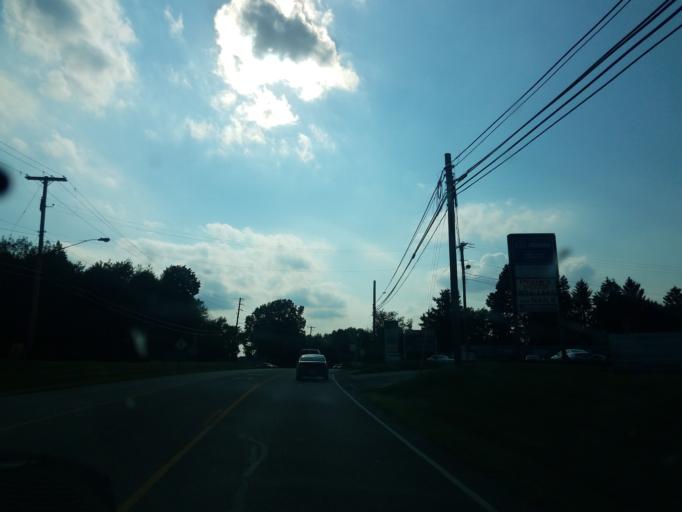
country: US
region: Ohio
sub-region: Stark County
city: Canal Fulton
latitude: 40.8825
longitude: -81.5760
